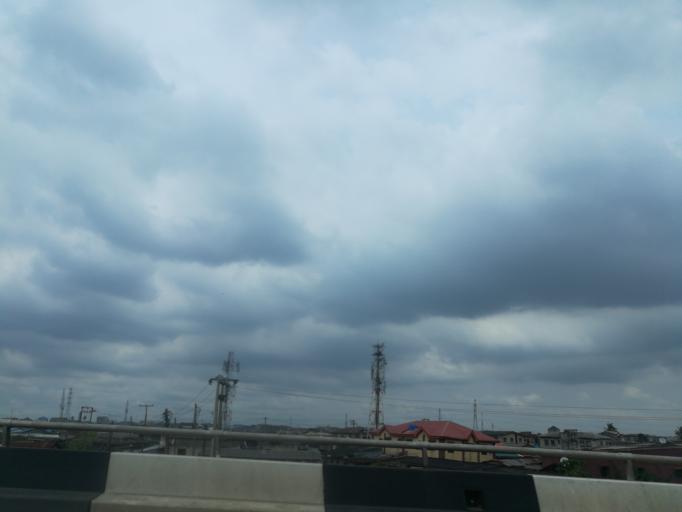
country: NG
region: Lagos
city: Somolu
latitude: 6.5368
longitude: 3.4002
